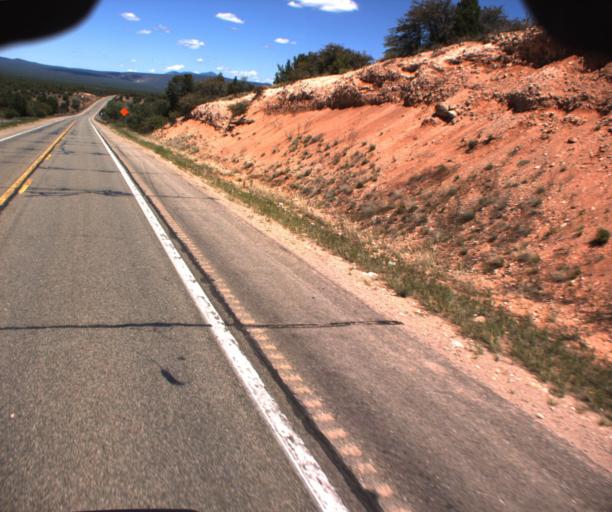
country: US
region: Arizona
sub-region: Yavapai County
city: Paulden
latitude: 34.9751
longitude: -112.4046
